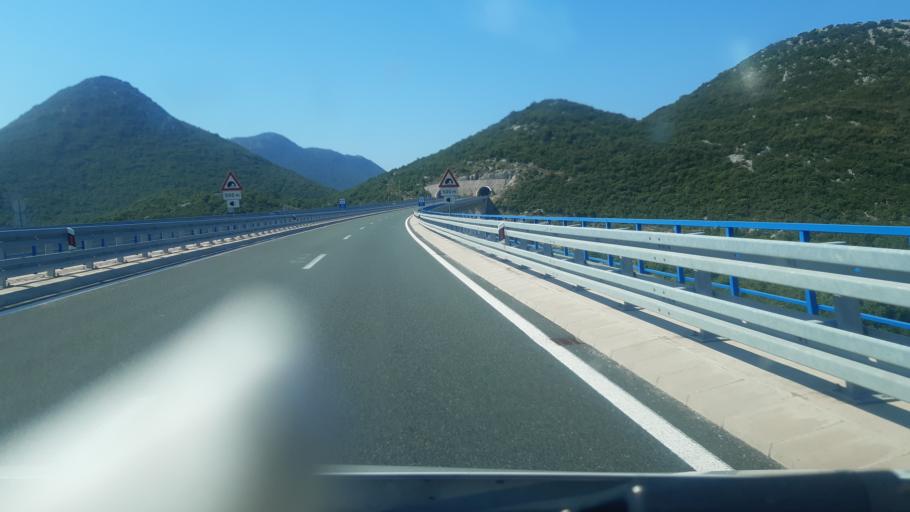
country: HR
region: Dubrovacko-Neretvanska
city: Komin
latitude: 43.1198
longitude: 17.4838
